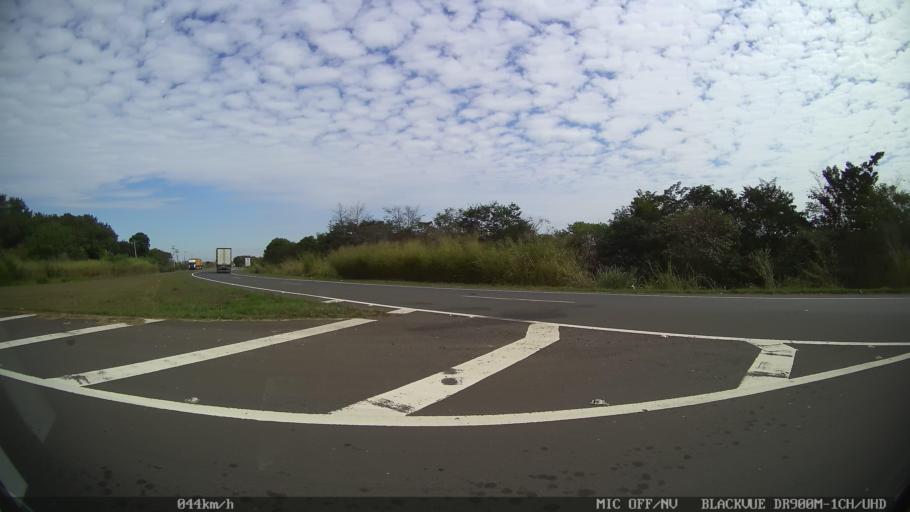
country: BR
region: Sao Paulo
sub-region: Santa Barbara D'Oeste
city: Santa Barbara d'Oeste
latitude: -22.7718
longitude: -47.4229
